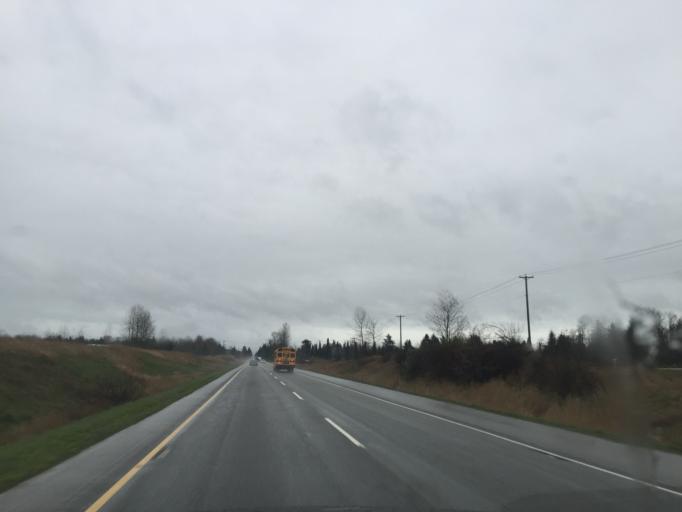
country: CA
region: British Columbia
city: Aldergrove
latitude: 49.0862
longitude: -122.4543
